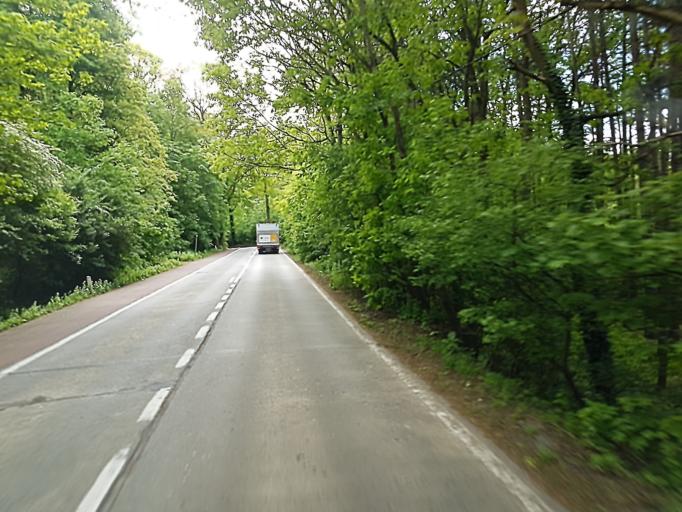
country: BE
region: Flanders
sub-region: Provincie Vlaams-Brabant
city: Diest
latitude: 50.9957
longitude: 5.0324
